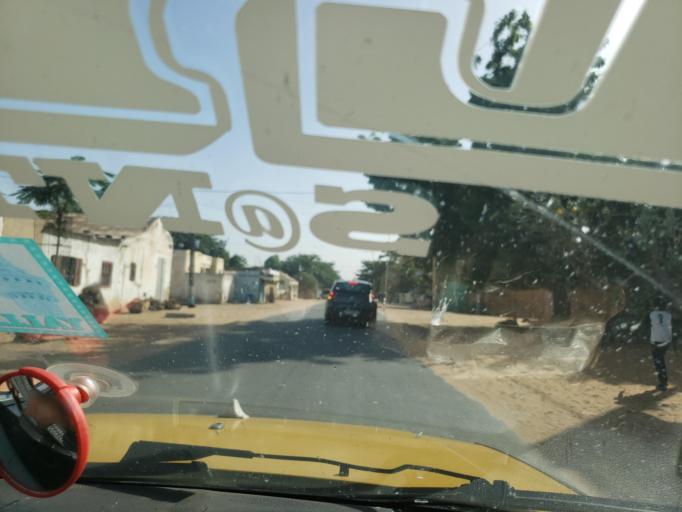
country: SN
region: Louga
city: Louga
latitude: 15.6244
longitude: -16.2140
